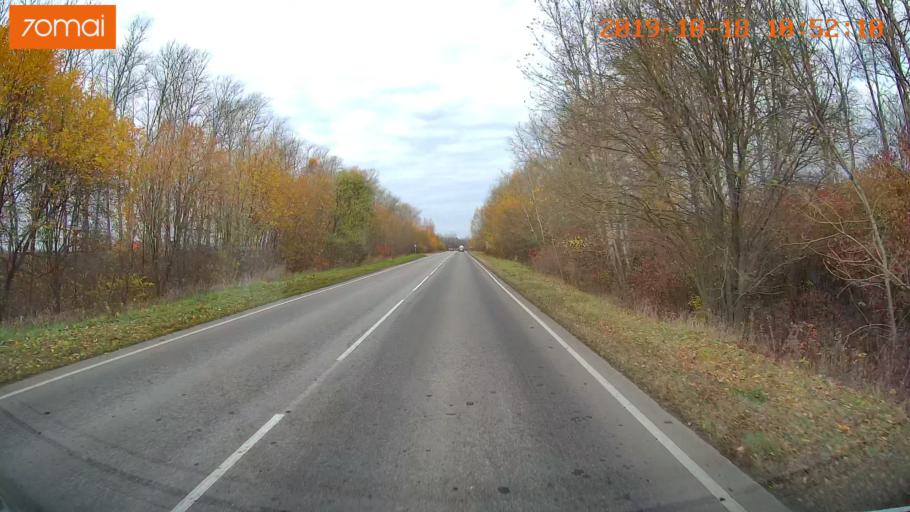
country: RU
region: Tula
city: Yepifan'
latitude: 53.7632
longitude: 38.6558
